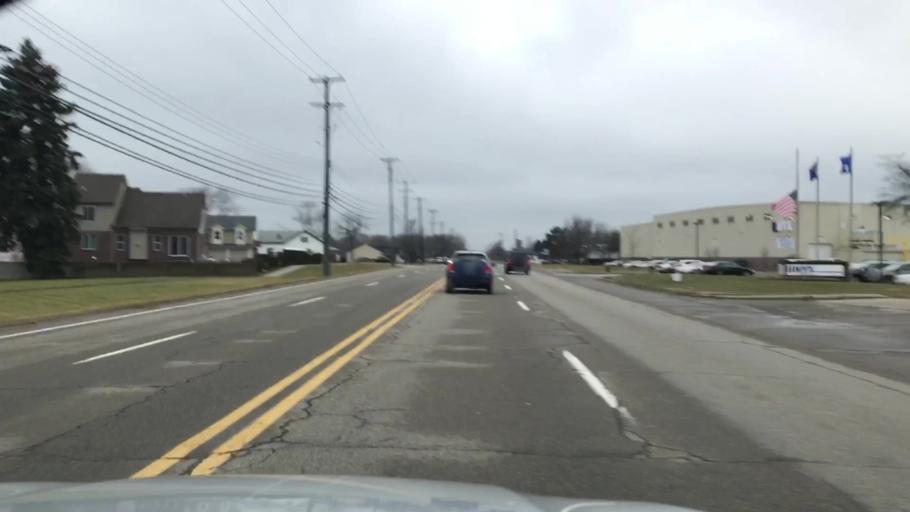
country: US
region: Michigan
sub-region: Wayne County
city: Plymouth
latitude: 42.3707
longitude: -83.4241
